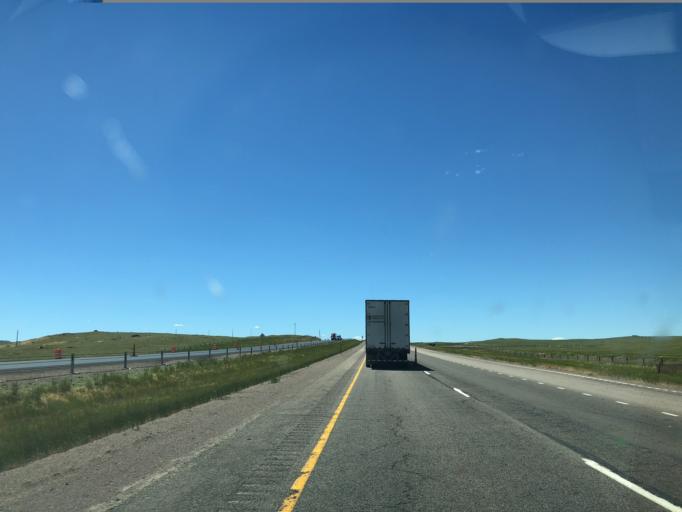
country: US
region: Wyoming
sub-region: Laramie County
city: Cheyenne
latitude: 41.0966
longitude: -105.1840
